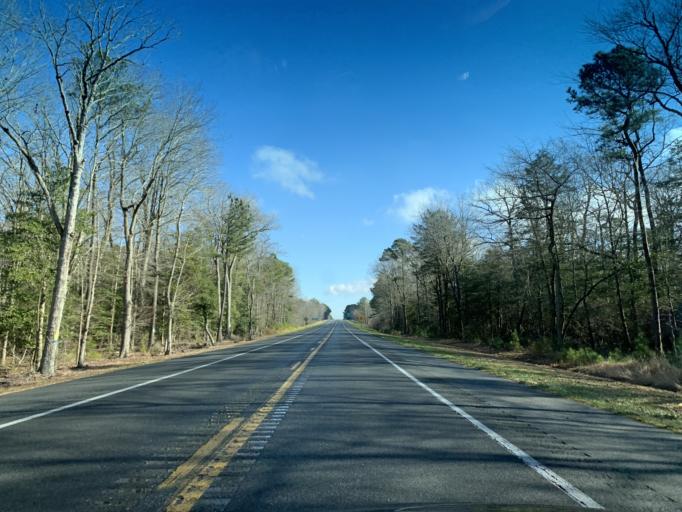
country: US
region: Maryland
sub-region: Worcester County
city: Berlin
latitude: 38.3771
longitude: -75.2200
